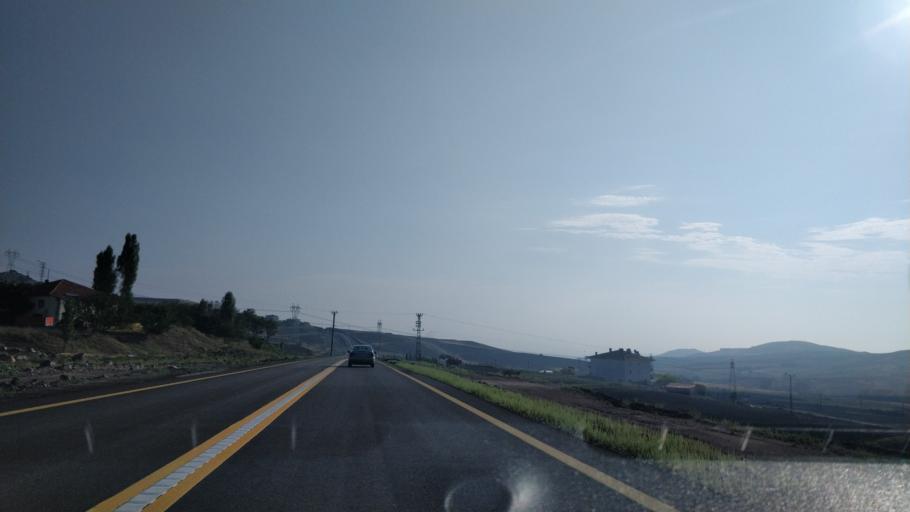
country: TR
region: Ankara
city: Etimesgut
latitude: 39.8615
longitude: 32.5822
